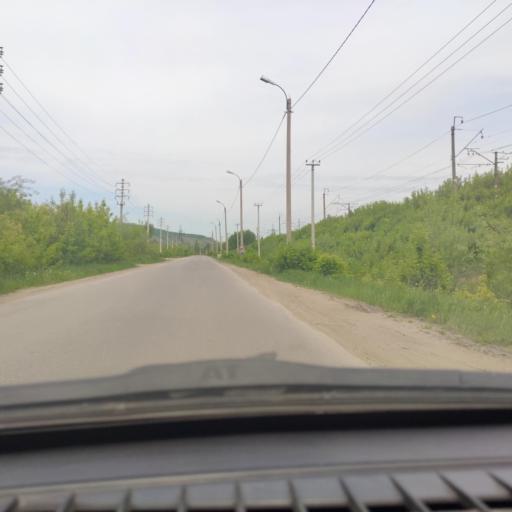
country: RU
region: Samara
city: Zhigulevsk
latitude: 53.4093
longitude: 49.4862
